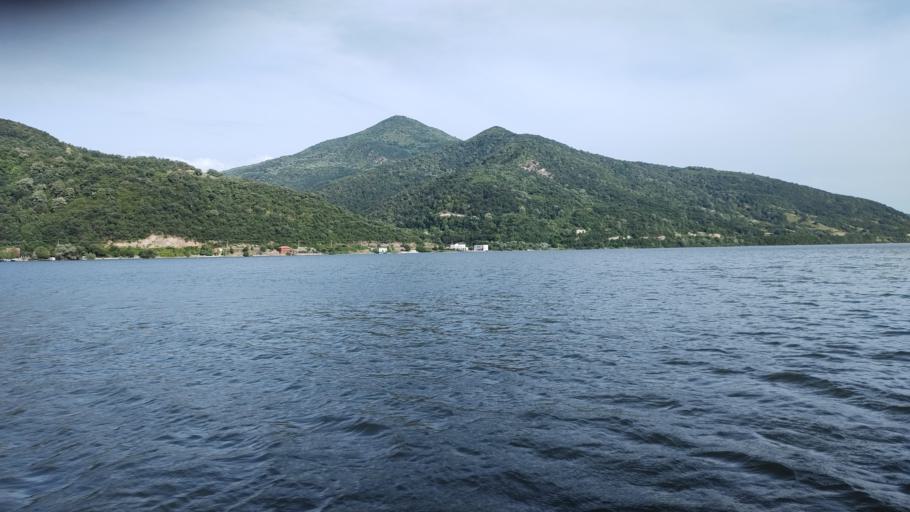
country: RO
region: Caras-Severin
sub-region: Comuna Berzasca
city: Berzasca
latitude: 44.5875
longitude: 22.0246
